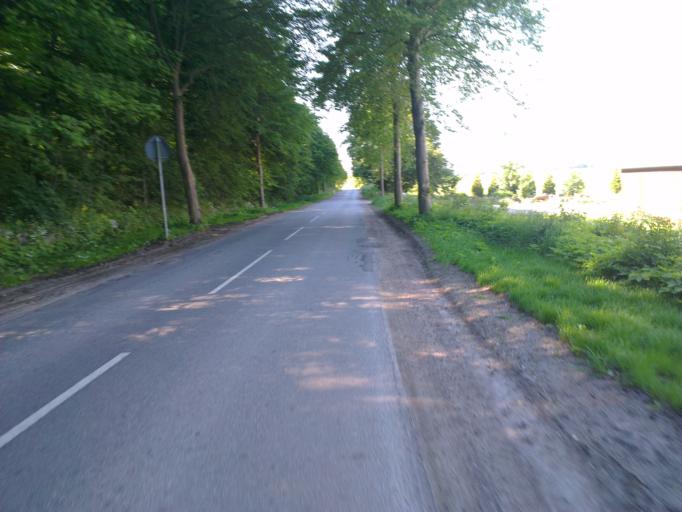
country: DK
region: Capital Region
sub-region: Frederikssund Kommune
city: Skibby
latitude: 55.7817
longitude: 11.9425
